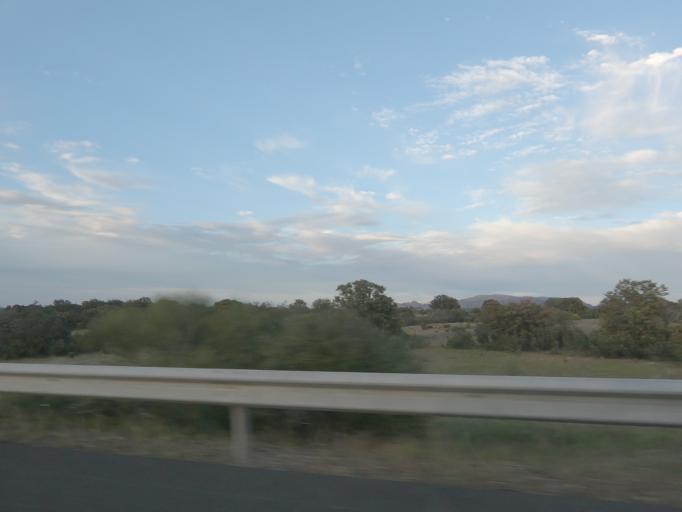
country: ES
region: Extremadura
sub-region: Provincia de Caceres
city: Alcuescar
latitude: 39.1877
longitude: -6.2764
